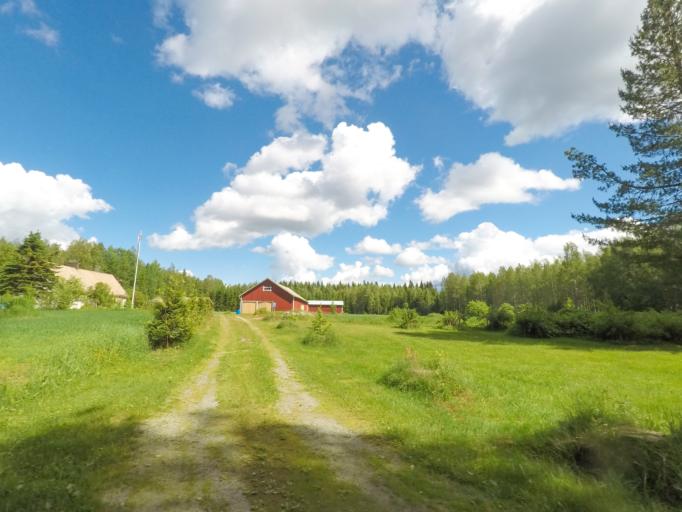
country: FI
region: Central Finland
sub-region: Jyvaeskylae
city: Hankasalmi
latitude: 62.4369
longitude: 26.6467
